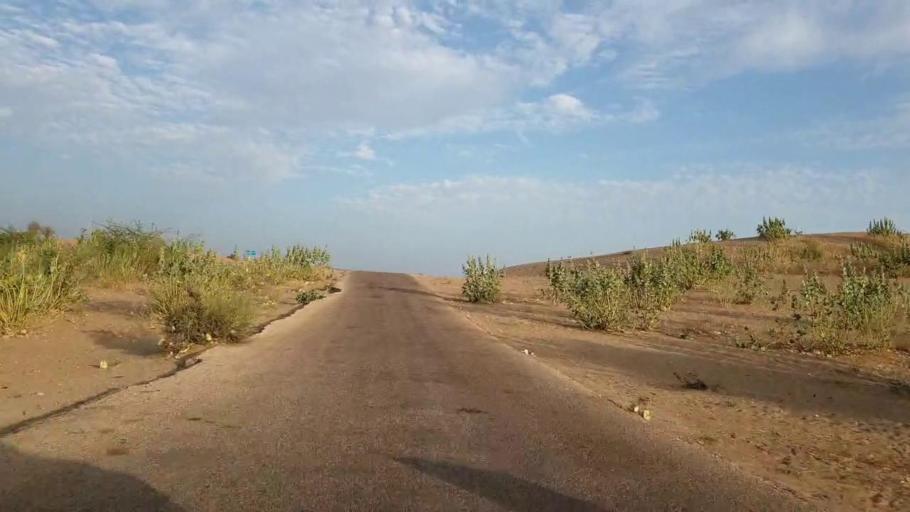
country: PK
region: Sindh
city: Umarkot
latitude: 25.1512
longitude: 70.0106
